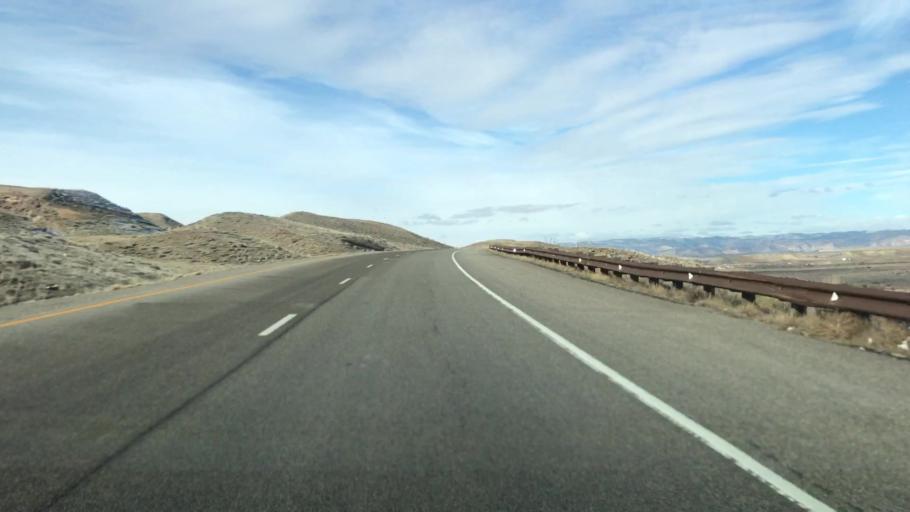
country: US
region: Colorado
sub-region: Mesa County
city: Loma
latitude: 39.2256
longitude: -108.8959
